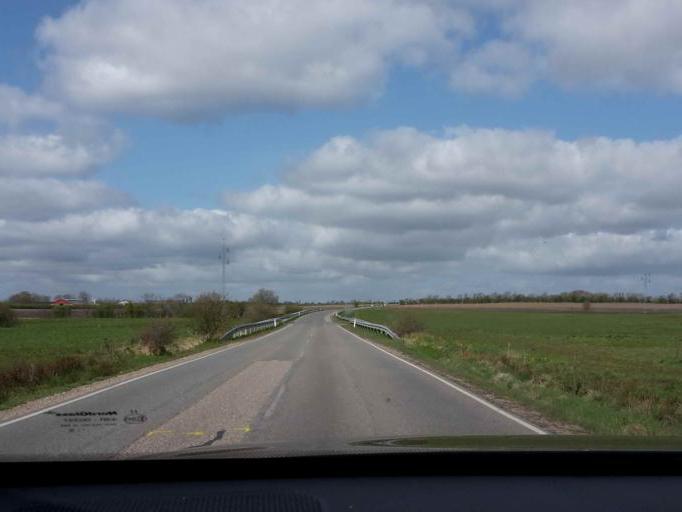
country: DK
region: South Denmark
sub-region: Varde Kommune
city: Olgod
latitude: 55.7912
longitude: 8.6782
